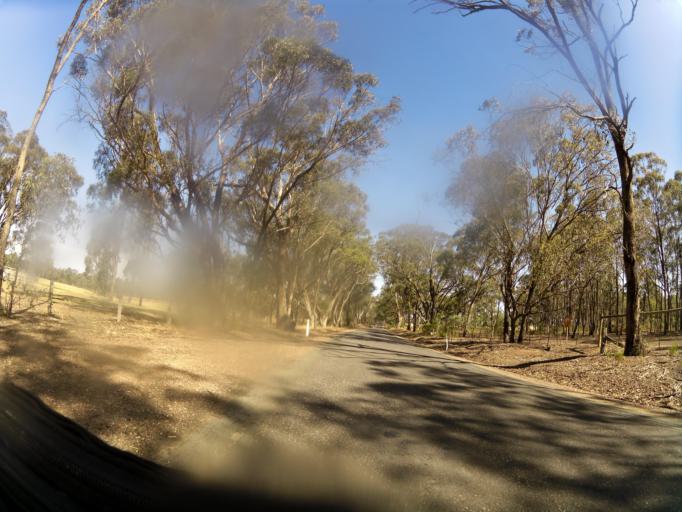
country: AU
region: Victoria
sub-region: Campaspe
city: Kyabram
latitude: -36.8838
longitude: 145.0971
